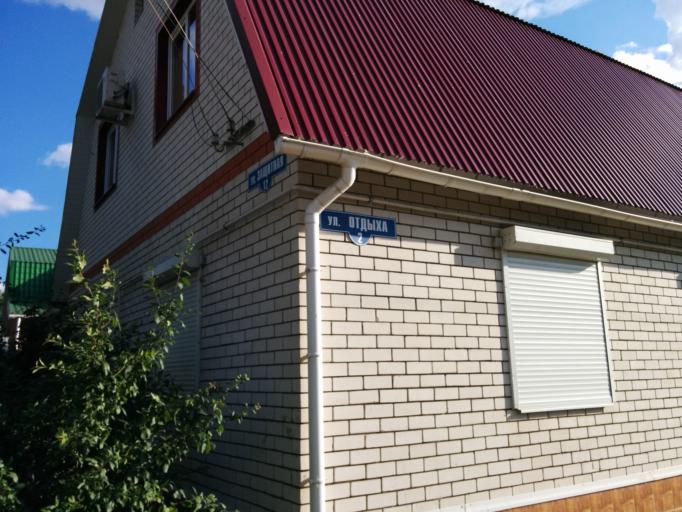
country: RU
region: Tambov
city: Tambov
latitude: 52.7500
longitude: 41.4404
